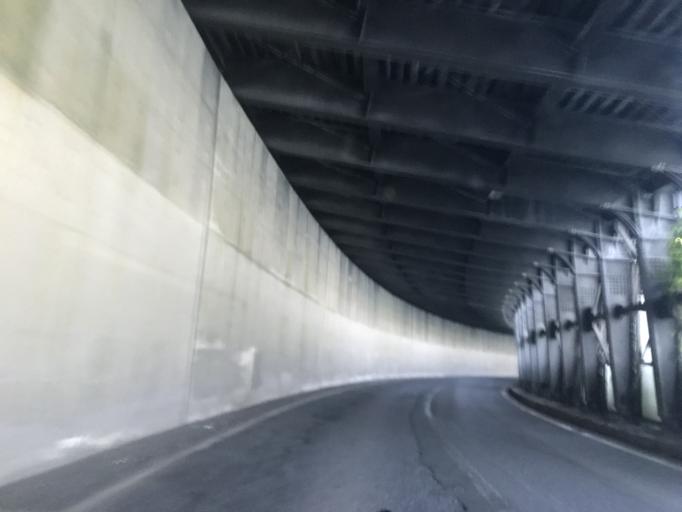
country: JP
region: Iwate
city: Kitakami
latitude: 39.3085
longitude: 140.8385
